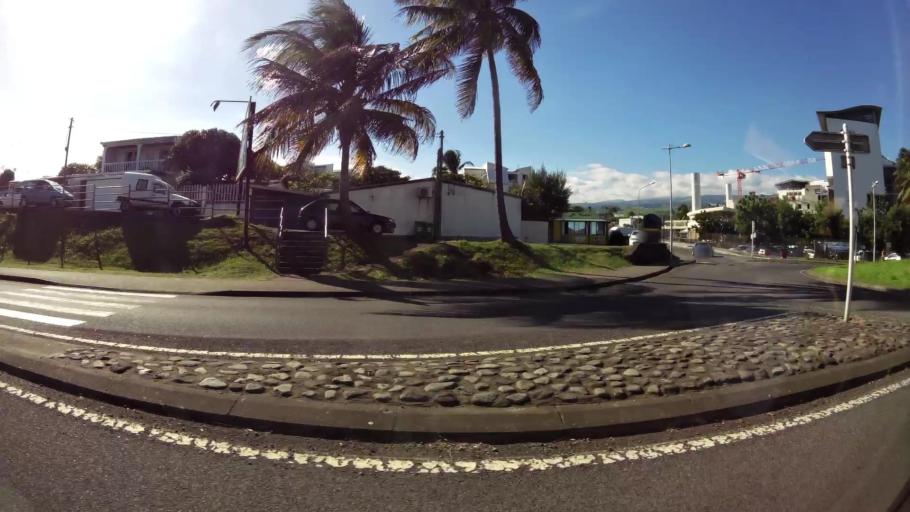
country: RE
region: Reunion
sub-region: Reunion
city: Saint-Pierre
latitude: -21.3470
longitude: 55.4906
